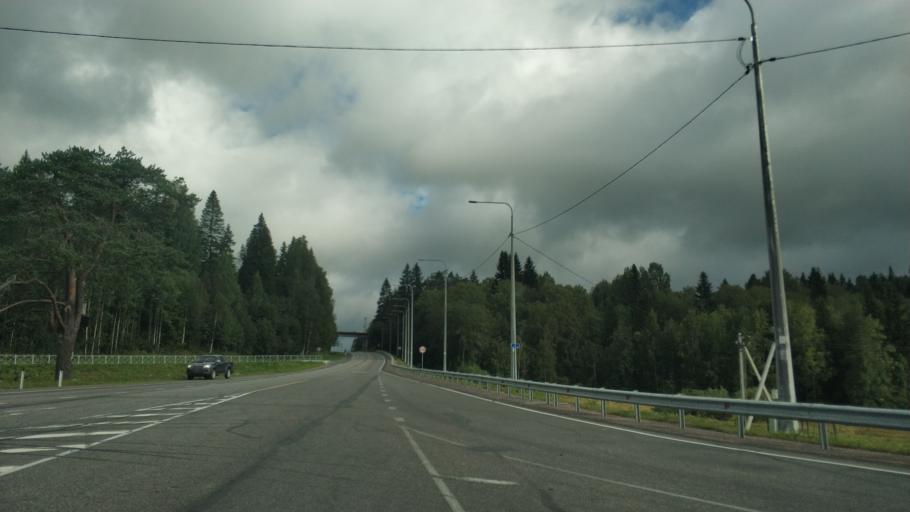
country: RU
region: Republic of Karelia
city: Khelyulya
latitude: 61.7757
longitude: 30.6620
